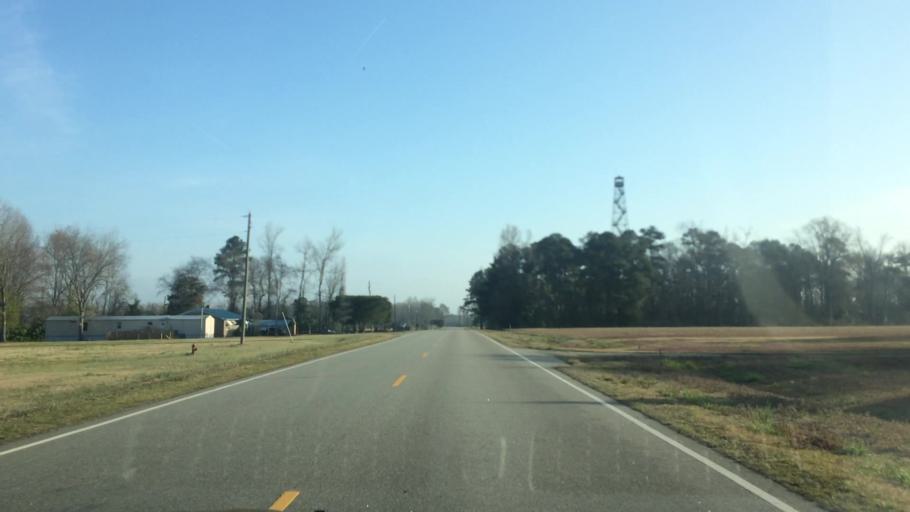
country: US
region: North Carolina
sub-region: Edgecombe County
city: Pinetops
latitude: 35.6938
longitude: -77.6391
